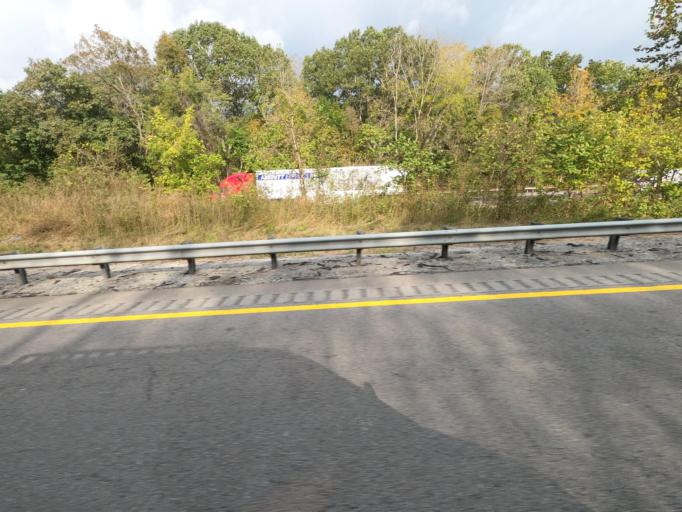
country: US
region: Tennessee
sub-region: Dickson County
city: Burns
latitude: 36.0204
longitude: -87.2312
